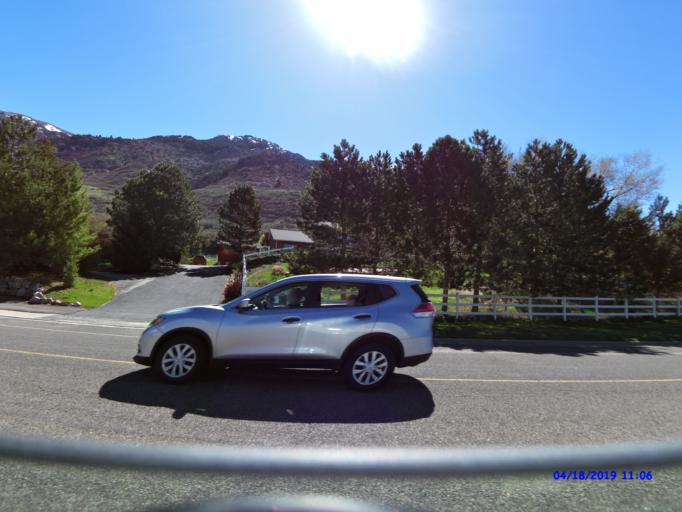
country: US
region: Utah
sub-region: Weber County
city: North Ogden
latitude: 41.2866
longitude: -111.9483
